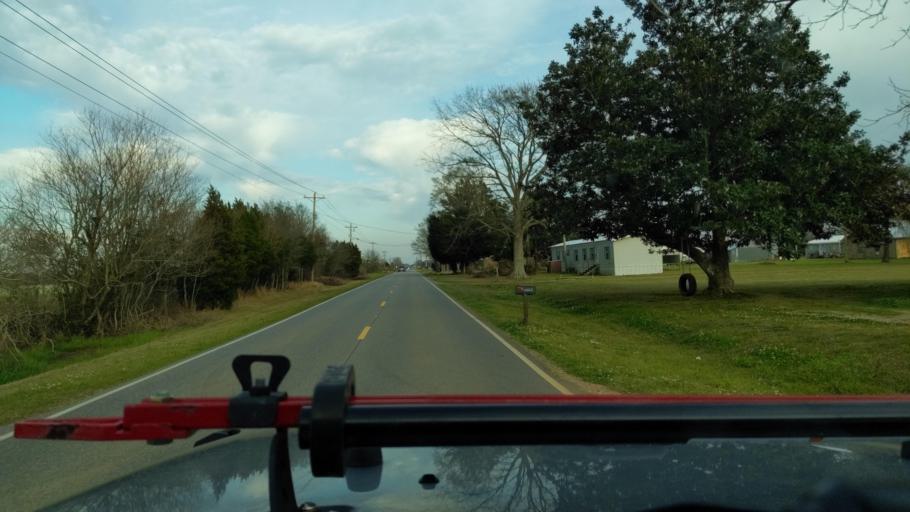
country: US
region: Alabama
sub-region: Baldwin County
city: Foley
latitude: 30.4580
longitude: -87.7130
